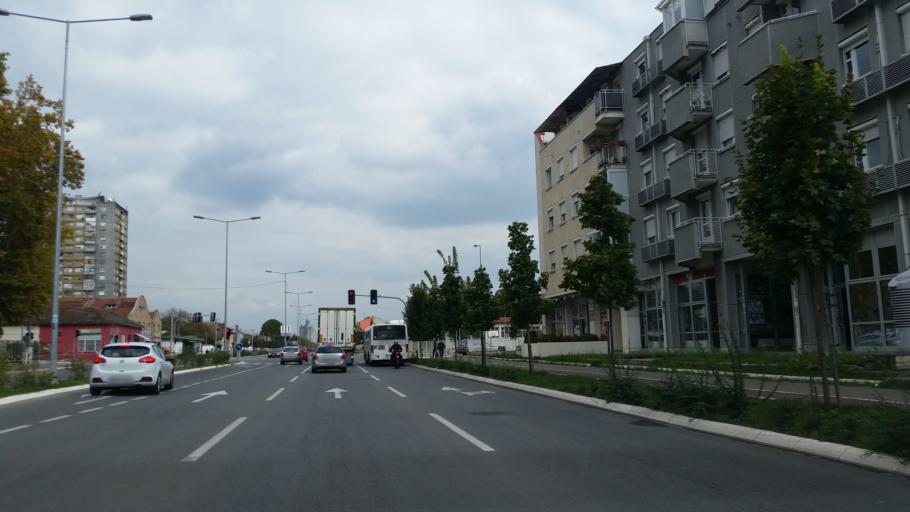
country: RS
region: Central Serbia
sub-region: Belgrade
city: Zemun
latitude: 44.8074
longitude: 20.3754
